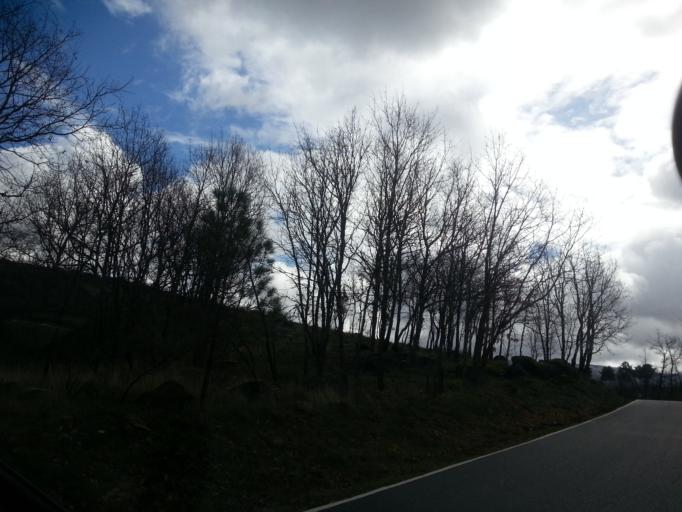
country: PT
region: Guarda
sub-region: Fornos de Algodres
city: Fornos de Algodres
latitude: 40.5854
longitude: -7.4836
